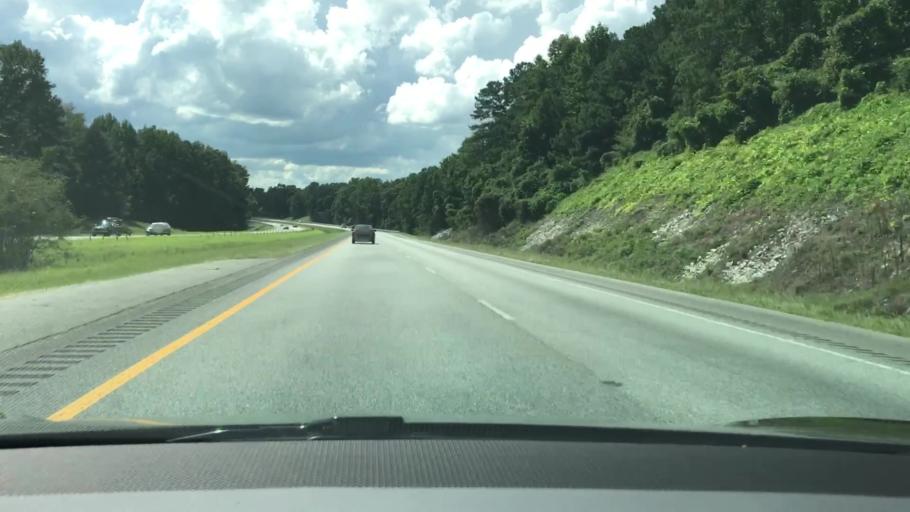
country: US
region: Alabama
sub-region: Macon County
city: Tuskegee
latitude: 32.4768
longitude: -85.6752
